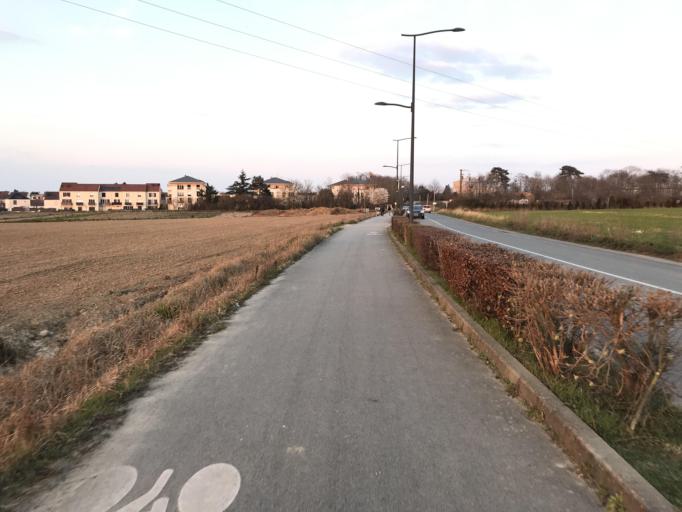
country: FR
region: Ile-de-France
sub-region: Departement de l'Essonne
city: Ballainvilliers
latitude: 48.6705
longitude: 2.2888
